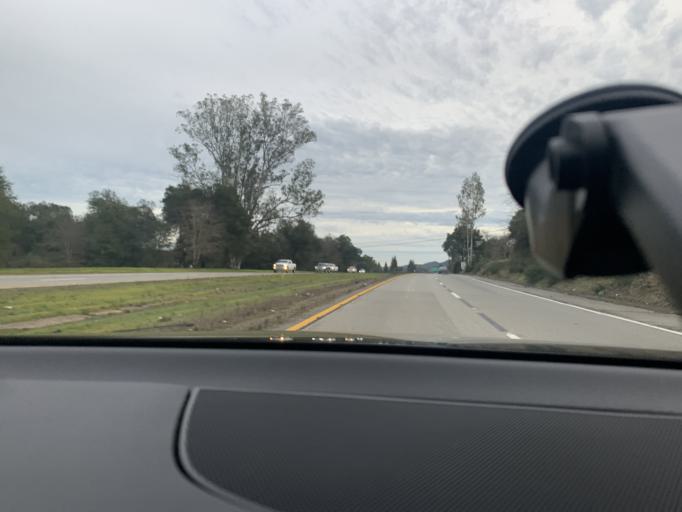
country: US
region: California
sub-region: Sonoma County
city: Cloverdale
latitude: 38.7738
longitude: -123.0003
